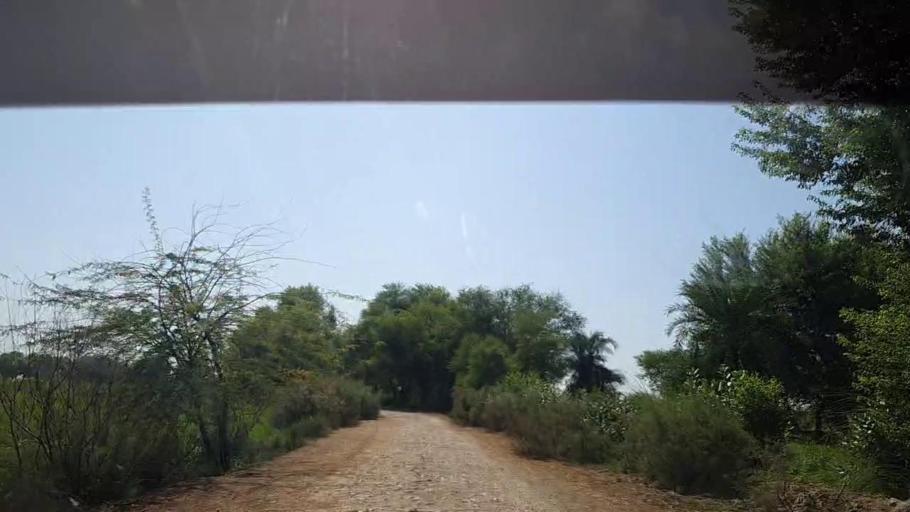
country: PK
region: Sindh
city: Ghauspur
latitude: 28.2128
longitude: 69.0845
